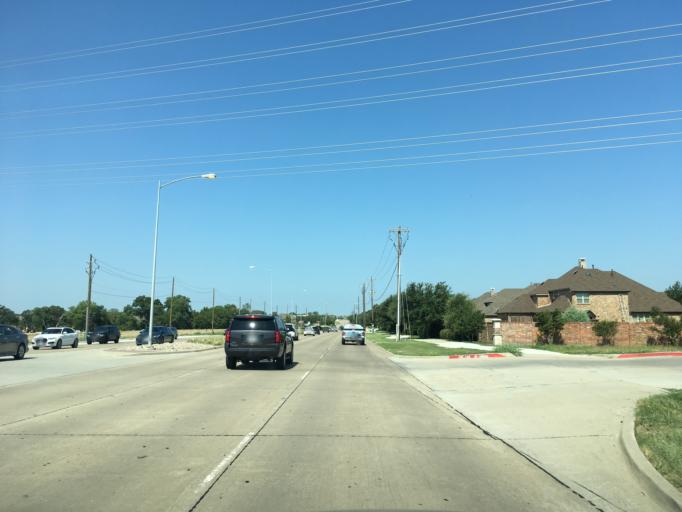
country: US
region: Texas
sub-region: Collin County
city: Allen
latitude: 33.1300
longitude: -96.6655
